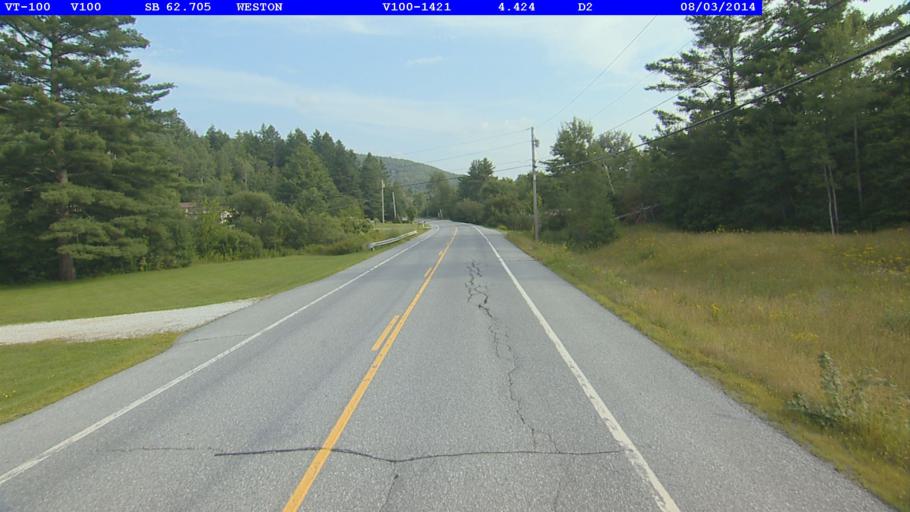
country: US
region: Vermont
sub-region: Windsor County
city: Chester
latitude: 43.3079
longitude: -72.7868
